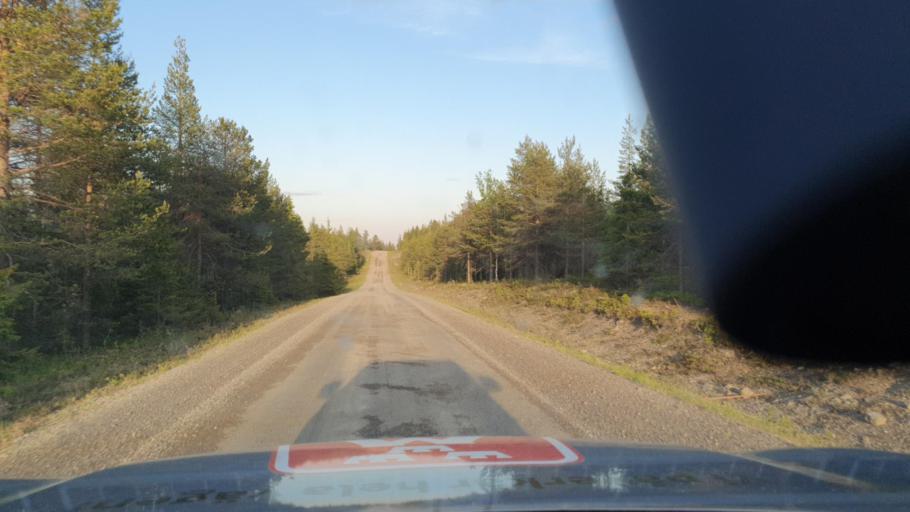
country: SE
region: Norrbotten
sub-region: Bodens Kommun
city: Boden
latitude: 66.4360
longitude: 21.7017
